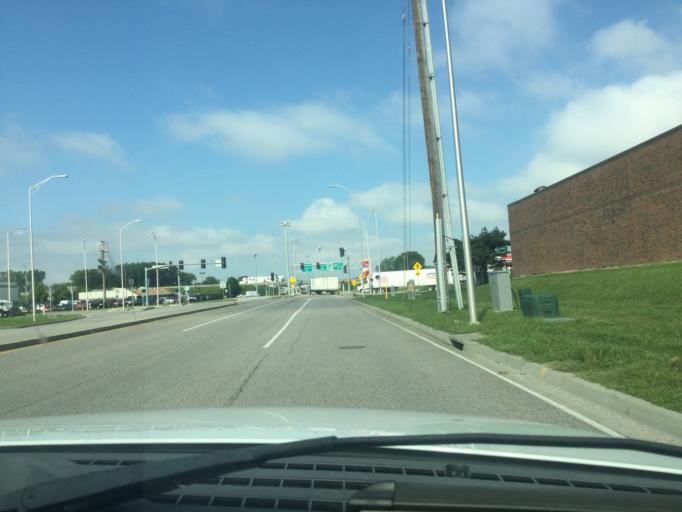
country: US
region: Missouri
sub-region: Jackson County
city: Sugar Creek
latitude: 39.1300
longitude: -94.4950
